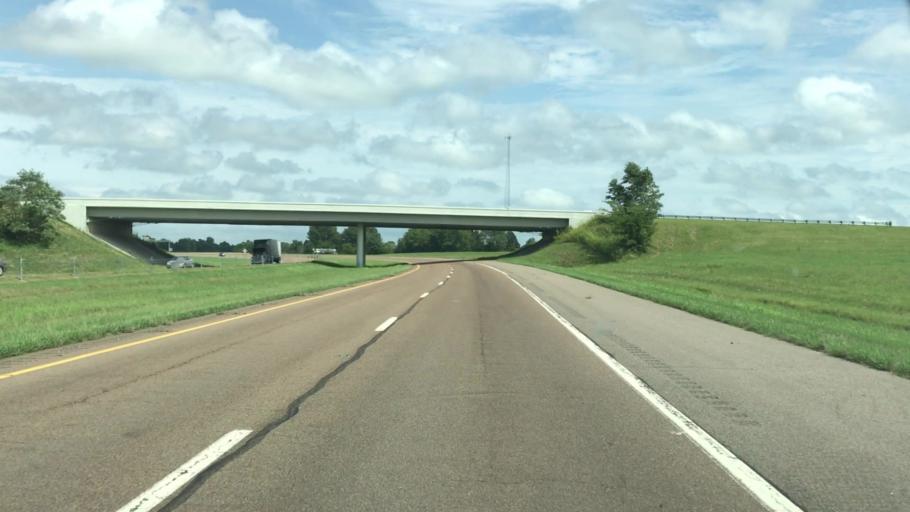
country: US
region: Tennessee
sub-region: Obion County
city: Union City
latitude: 36.4436
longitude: -89.0139
